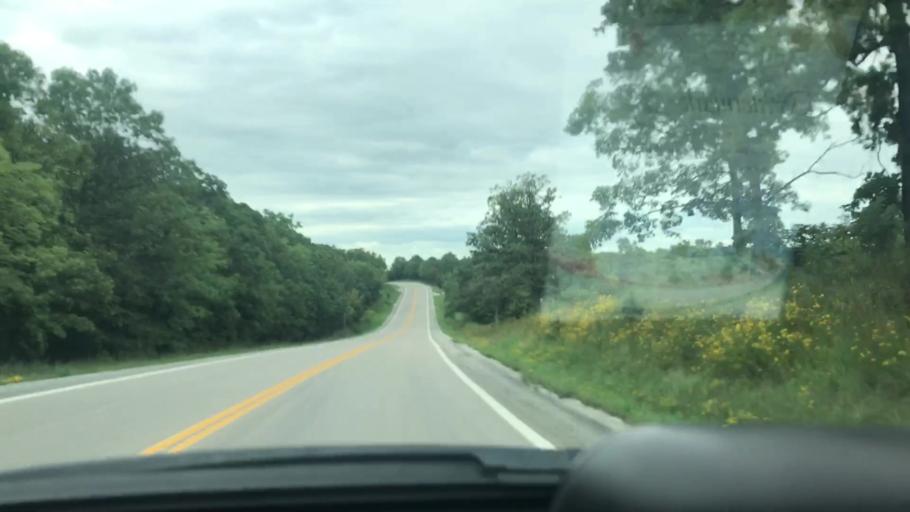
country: US
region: Missouri
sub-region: Benton County
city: Warsaw
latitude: 38.1663
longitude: -93.3084
